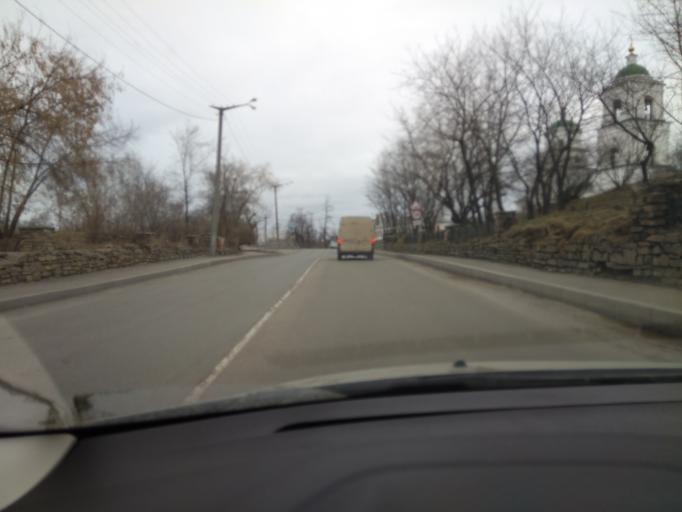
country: RU
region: Chelyabinsk
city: Kyshtym
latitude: 55.7037
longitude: 60.5303
